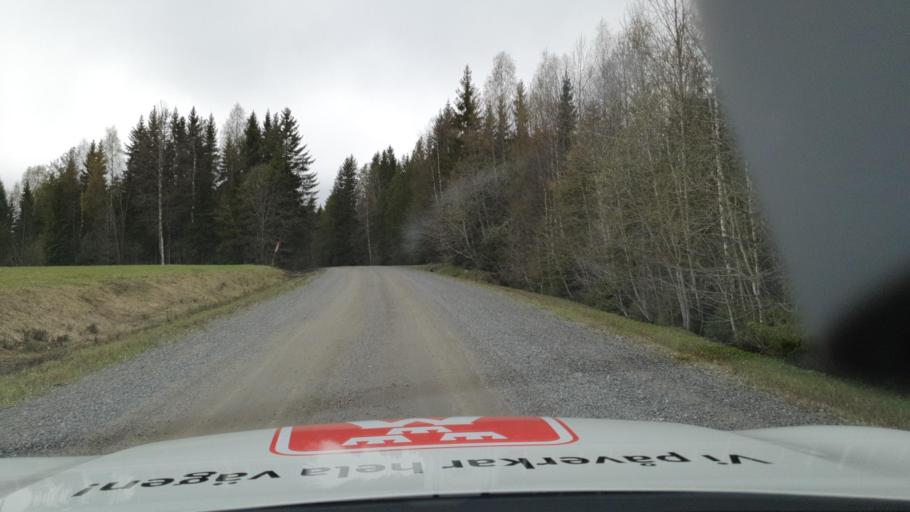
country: SE
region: Vaesterbotten
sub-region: Bjurholms Kommun
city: Bjurholm
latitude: 63.7957
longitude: 19.3361
